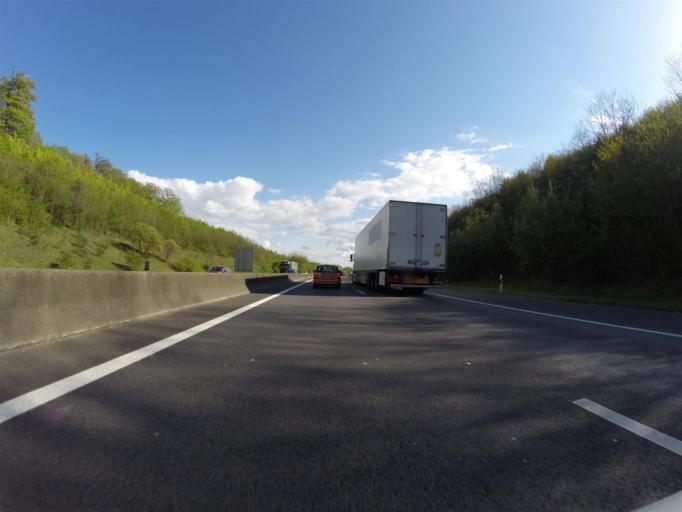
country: LU
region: Luxembourg
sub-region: Canton de Luxembourg
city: Hesperange
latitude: 49.5625
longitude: 6.1297
